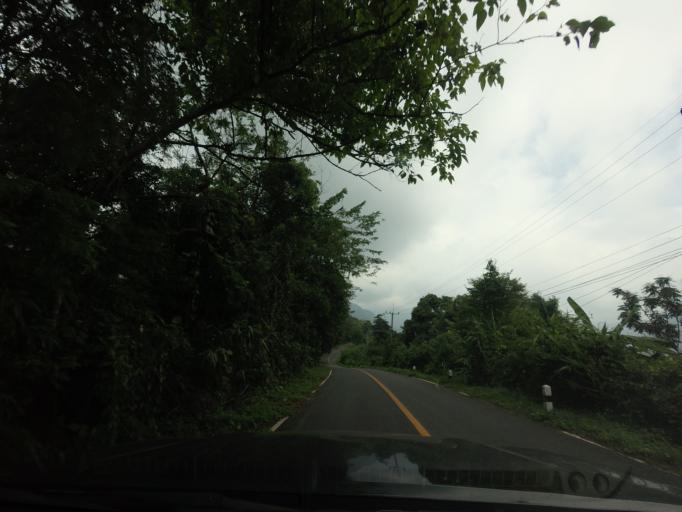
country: TH
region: Nan
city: Pua
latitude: 19.1879
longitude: 101.0367
